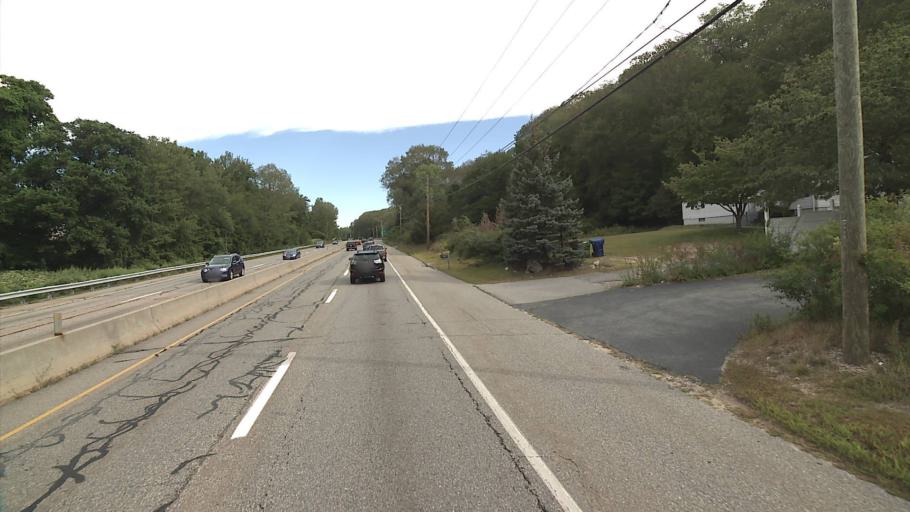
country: US
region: Connecticut
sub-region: New London County
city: Uncasville
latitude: 41.4057
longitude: -72.1061
